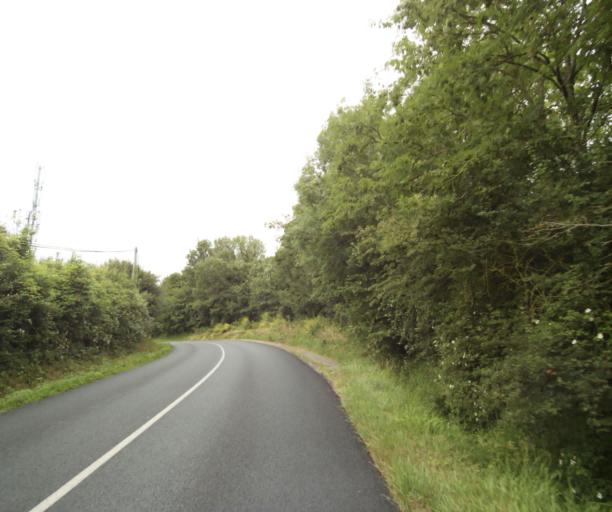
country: FR
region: Lower Normandy
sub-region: Departement du Calvados
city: Houlgate
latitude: 49.2831
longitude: -0.0818
